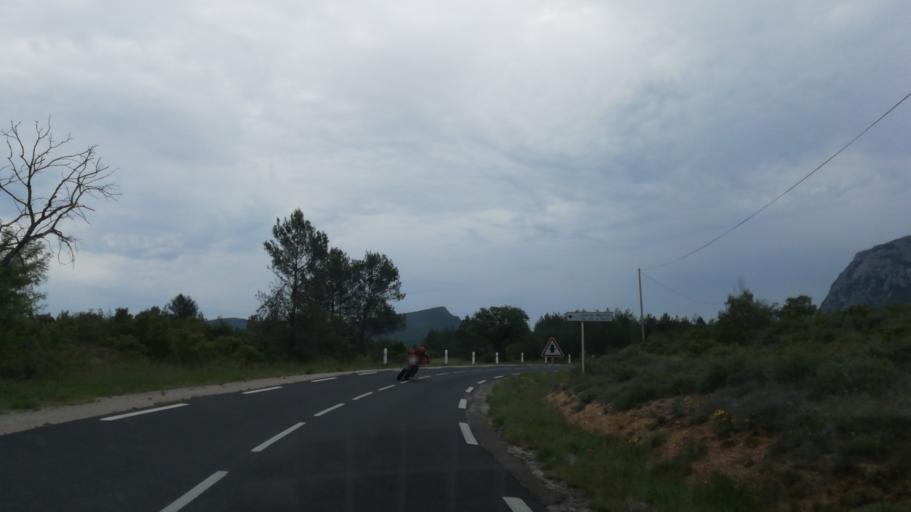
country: FR
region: Languedoc-Roussillon
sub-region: Departement de l'Herault
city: Saint-Martin-de-Londres
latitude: 43.7947
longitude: 3.7821
